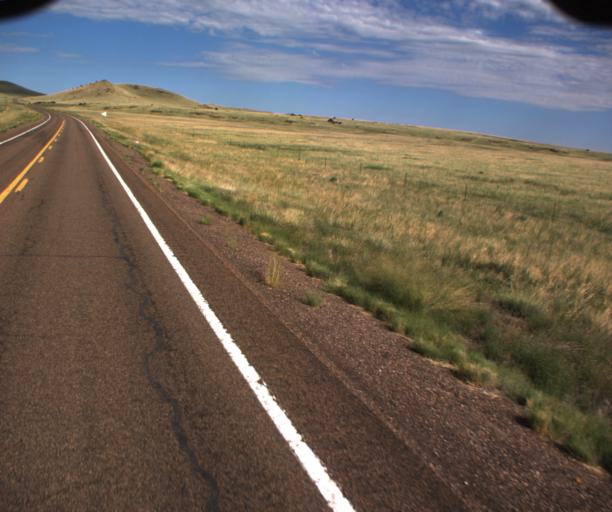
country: US
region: Arizona
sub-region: Apache County
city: Springerville
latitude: 34.2011
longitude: -109.3994
